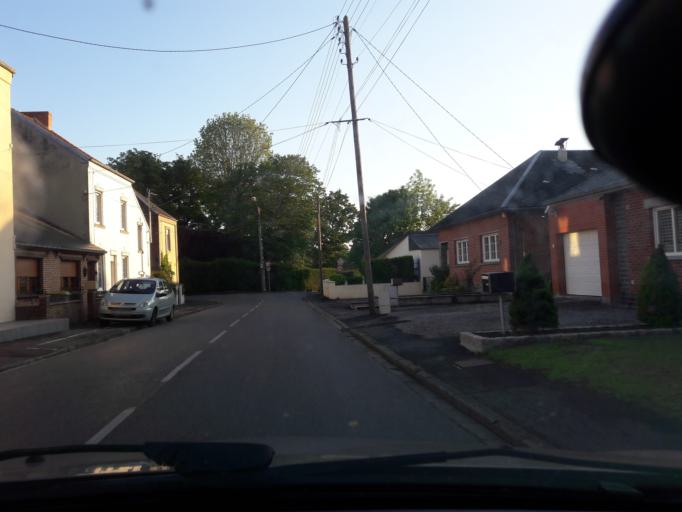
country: FR
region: Nord-Pas-de-Calais
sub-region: Departement du Nord
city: Marpent
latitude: 50.2876
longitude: 4.0721
